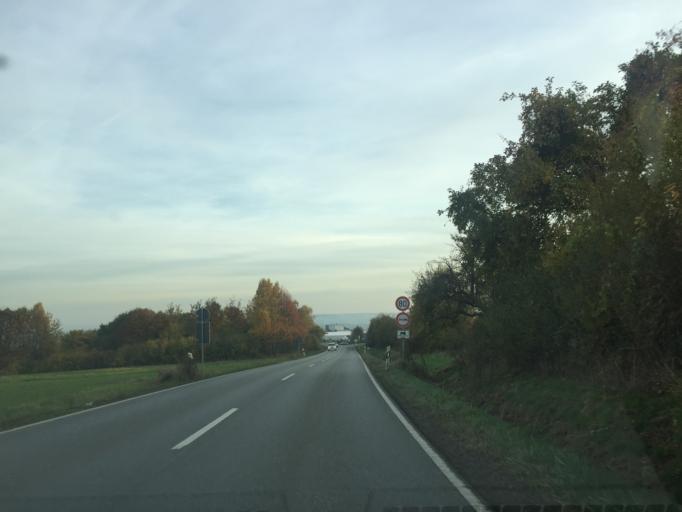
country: DE
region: Hesse
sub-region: Regierungsbezirk Giessen
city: Elz
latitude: 50.4285
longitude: 8.0161
